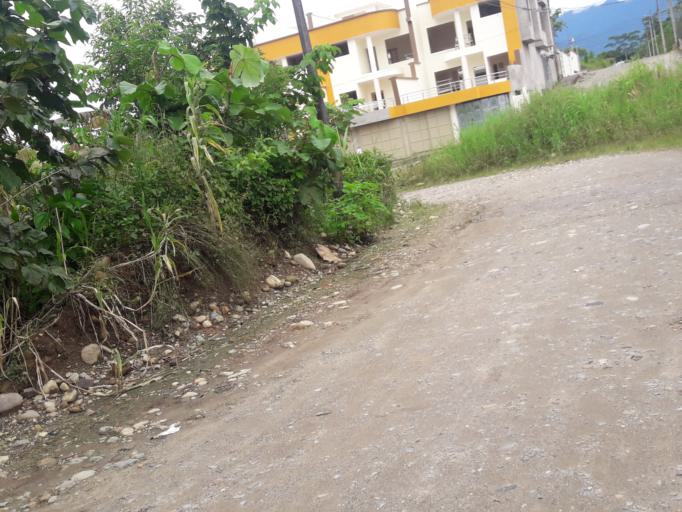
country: EC
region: Napo
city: Tena
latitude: -0.9832
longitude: -77.8234
